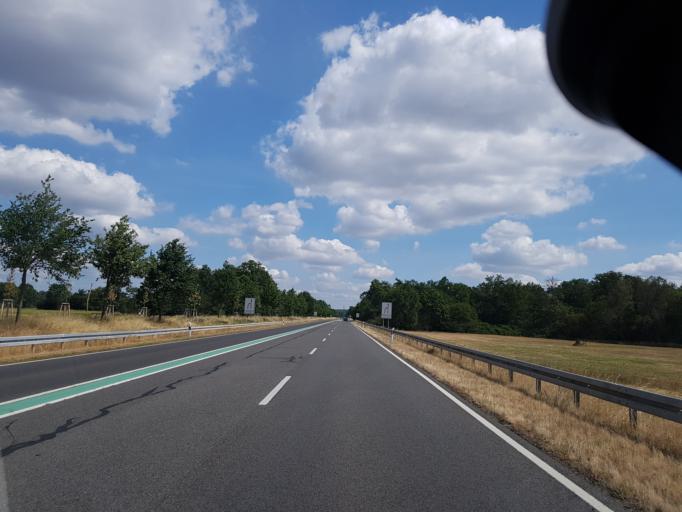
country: DE
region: Brandenburg
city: Drebkau
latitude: 51.6748
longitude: 14.2506
